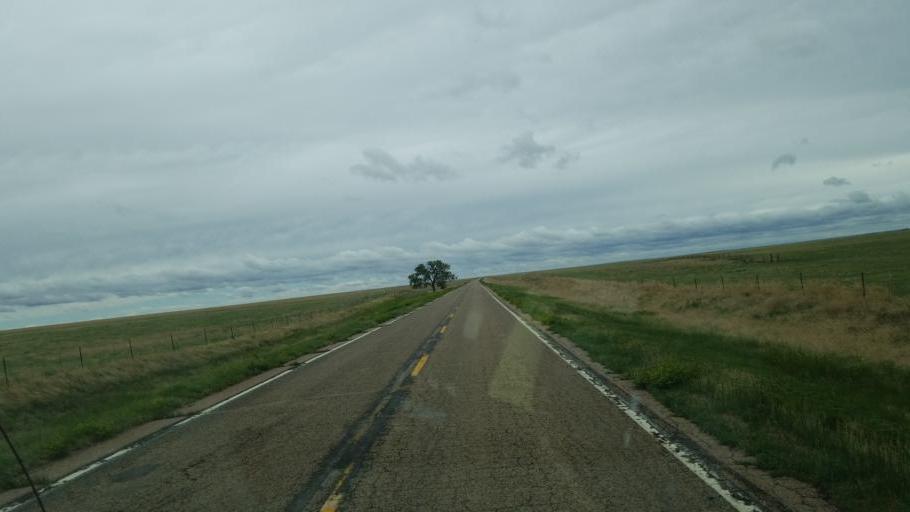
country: US
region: Colorado
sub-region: Lincoln County
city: Hugo
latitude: 38.8522
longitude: -103.7298
